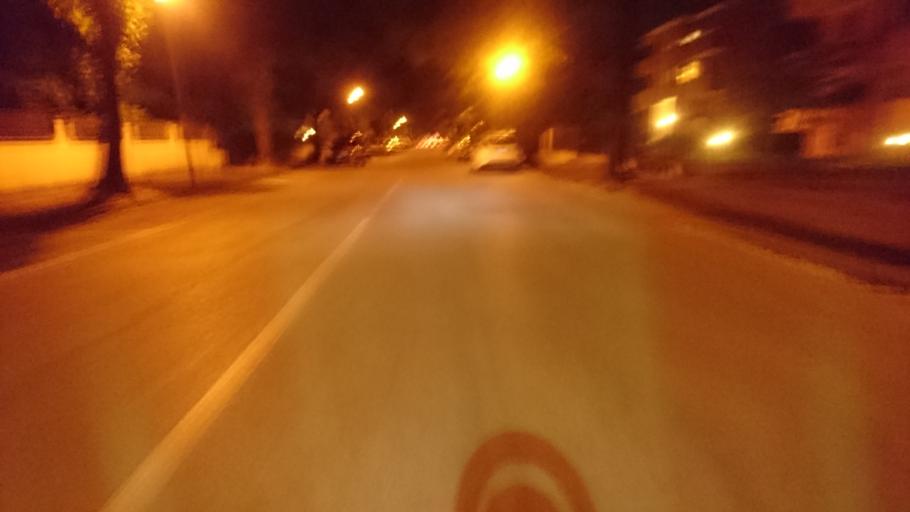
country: IT
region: Veneto
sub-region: Provincia di Padova
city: Abano Terme
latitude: 45.3565
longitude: 11.7795
